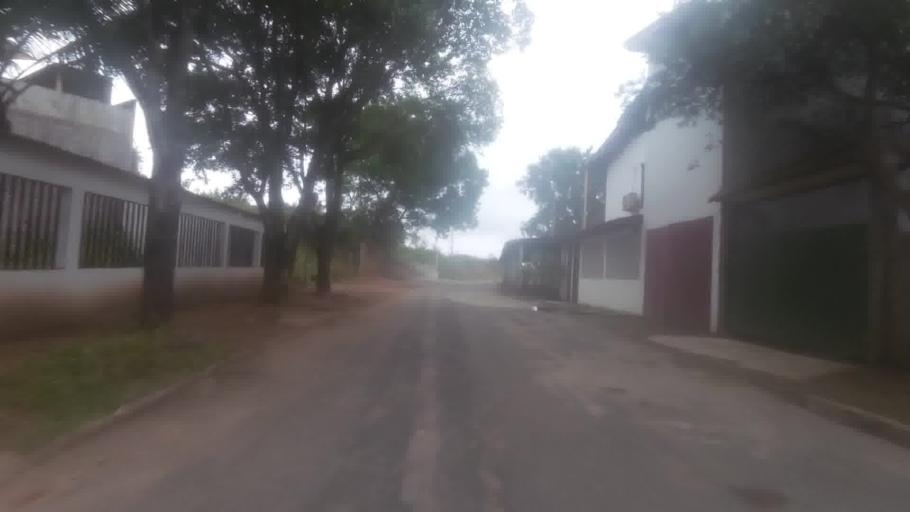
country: BR
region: Espirito Santo
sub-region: Piuma
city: Piuma
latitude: -20.8019
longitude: -40.5954
